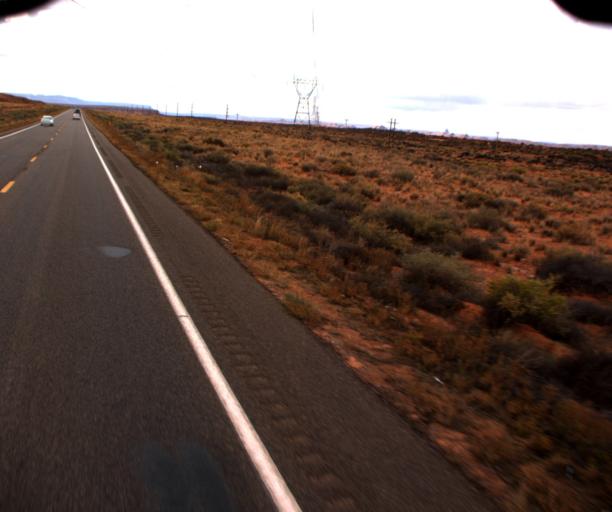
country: US
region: Arizona
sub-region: Navajo County
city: Kayenta
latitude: 36.8008
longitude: -109.9245
